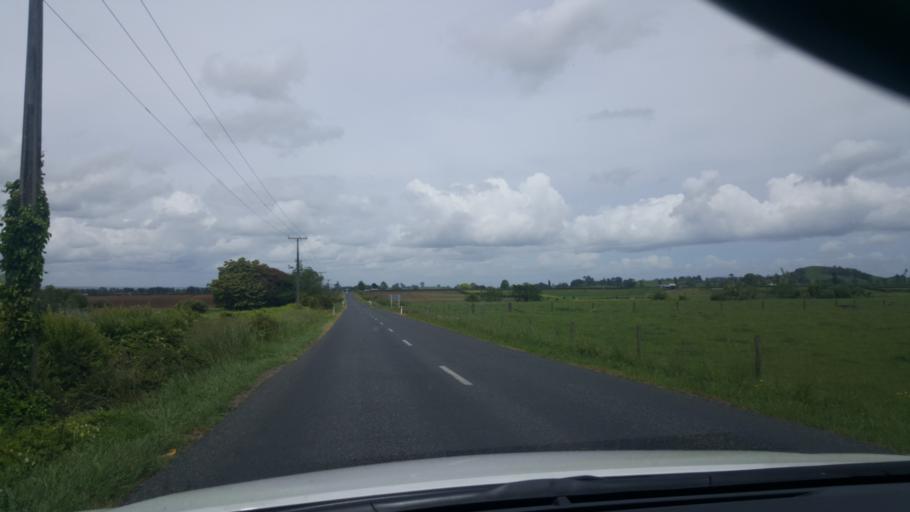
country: NZ
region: Waikato
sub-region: Matamata-Piako District
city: Matamata
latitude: -37.8742
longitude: 175.7254
